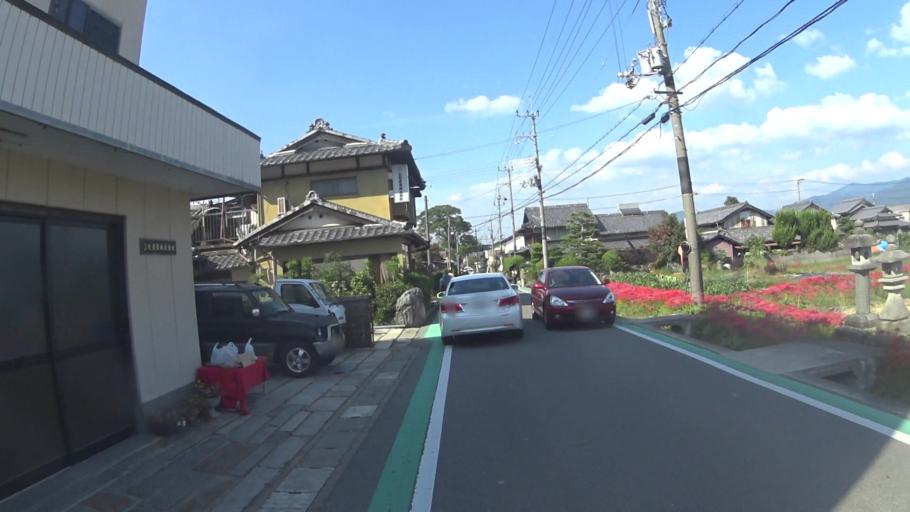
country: JP
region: Kyoto
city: Kameoka
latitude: 35.0035
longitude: 135.5494
